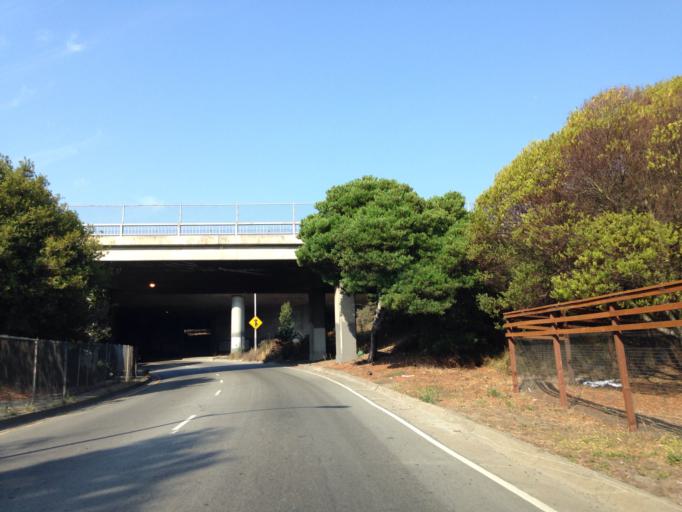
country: US
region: California
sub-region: San Mateo County
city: Brisbane
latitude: 37.7197
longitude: -122.3986
